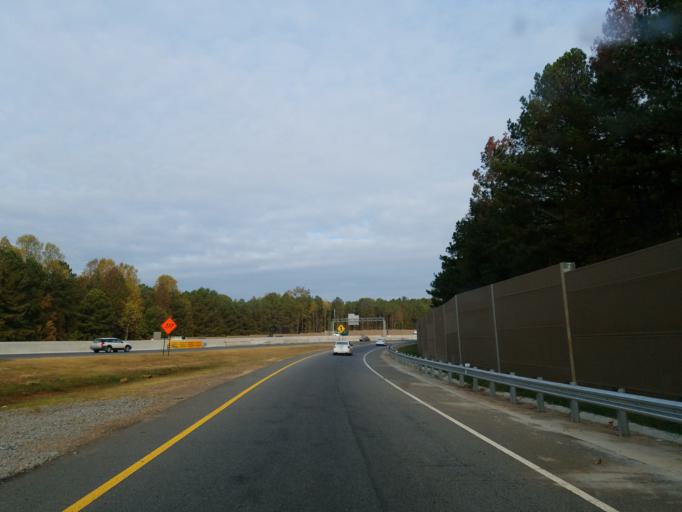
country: US
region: Georgia
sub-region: Cobb County
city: Kennesaw
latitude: 34.0407
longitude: -84.5626
